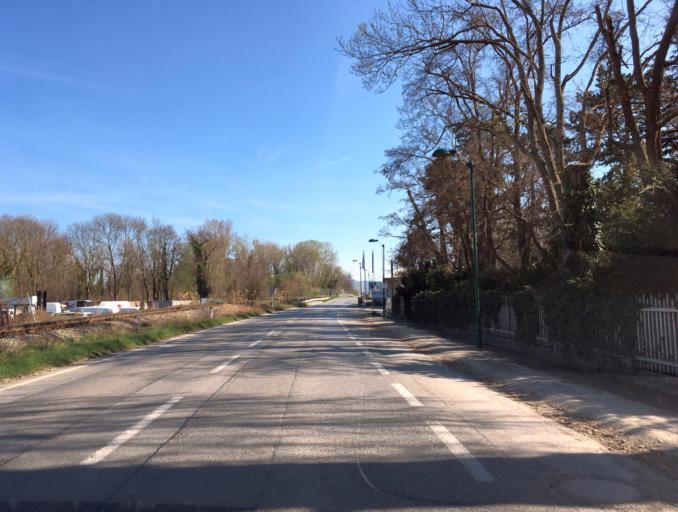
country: AT
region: Lower Austria
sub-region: Politischer Bezirk Bruck an der Leitha
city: Gotzendorf an der Leitha
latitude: 48.0125
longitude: 16.5830
